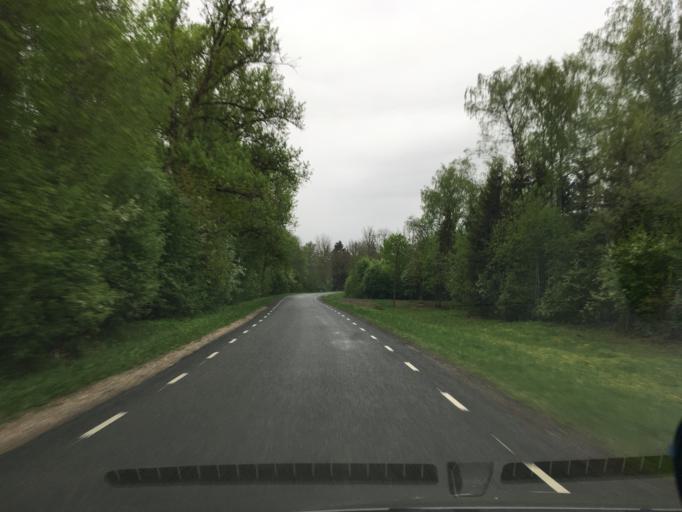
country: EE
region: Harju
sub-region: Keila linn
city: Keila
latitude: 59.2349
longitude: 24.4836
